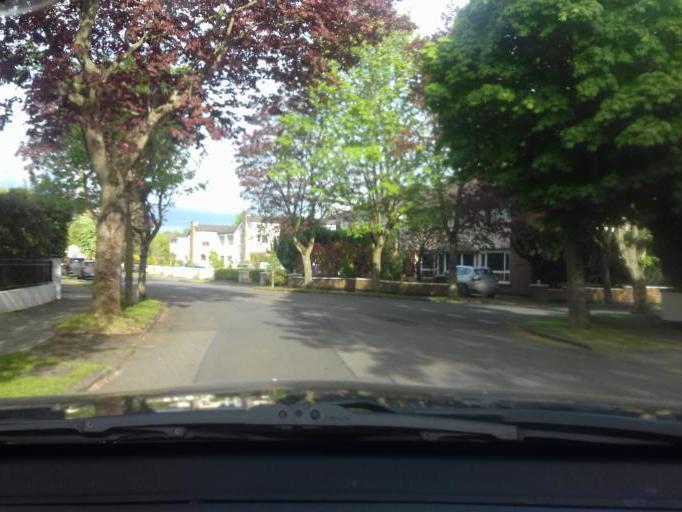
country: IE
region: Leinster
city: Castleknock
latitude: 53.3713
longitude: -6.3477
